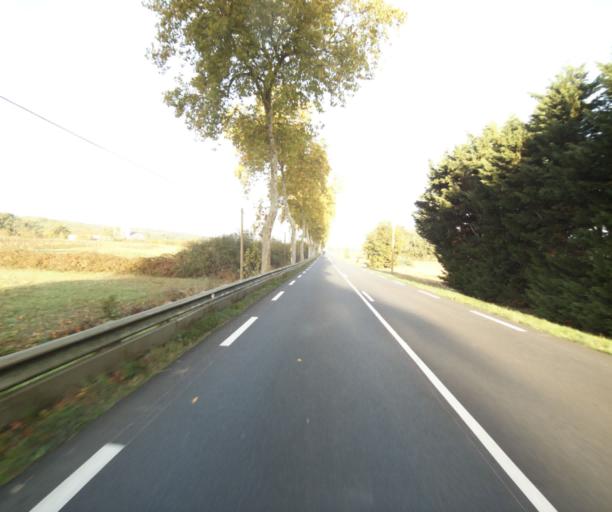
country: FR
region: Midi-Pyrenees
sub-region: Departement du Tarn-et-Garonne
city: Saint-Nauphary
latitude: 43.9386
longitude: 1.4767
